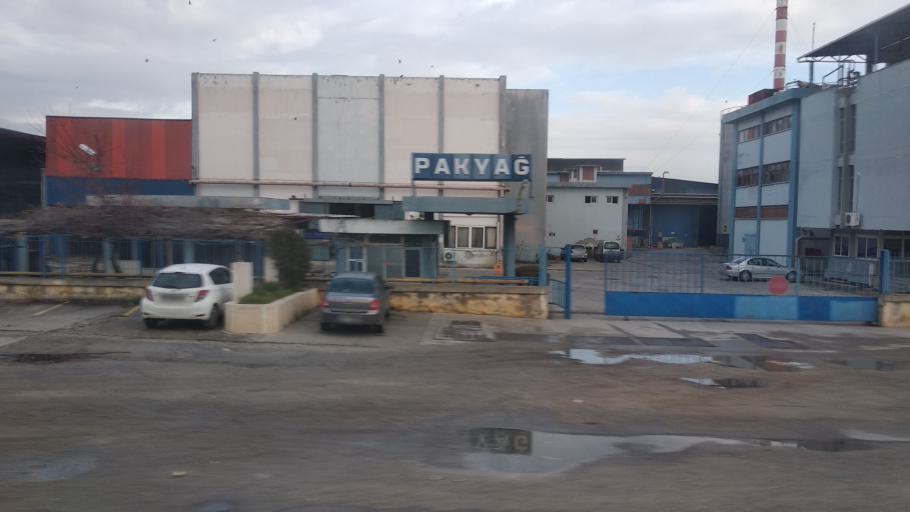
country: TR
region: Adana
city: Seyhan
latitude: 36.9948
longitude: 35.2115
